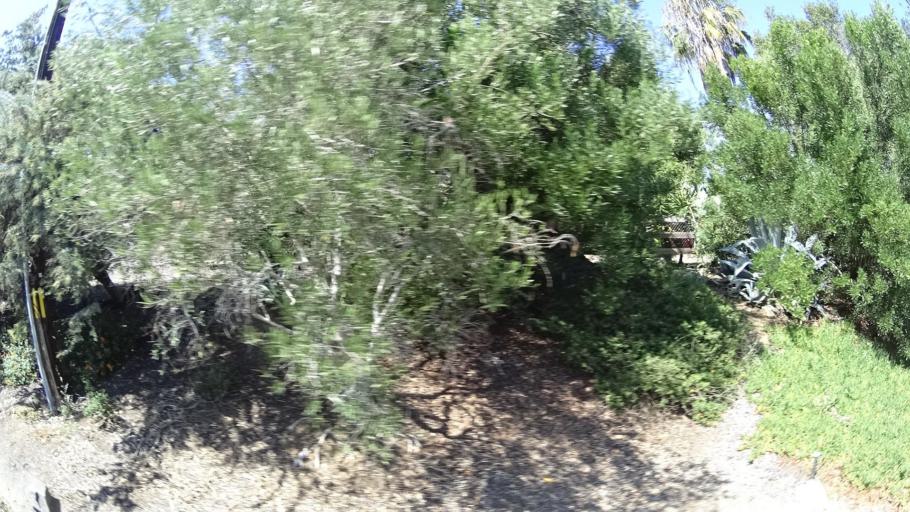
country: US
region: California
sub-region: San Diego County
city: Rancho Santa Fe
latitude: 33.0299
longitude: -117.2027
